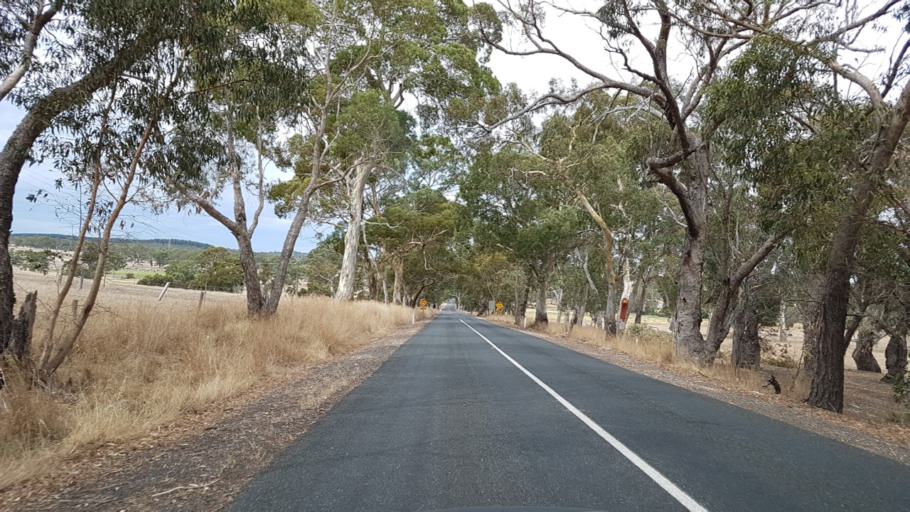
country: AU
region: South Australia
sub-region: Adelaide Hills
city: Birdwood
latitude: -34.7905
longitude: 138.9517
